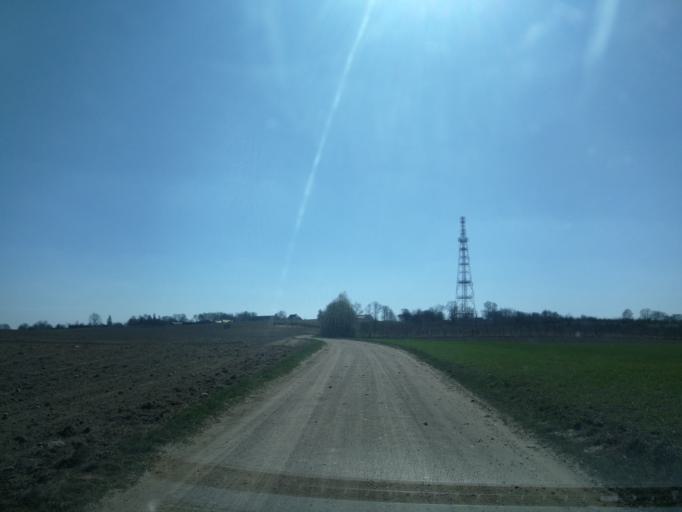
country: PL
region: Warmian-Masurian Voivodeship
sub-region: Powiat ostrodzki
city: Dabrowno
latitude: 53.4416
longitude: 19.9788
